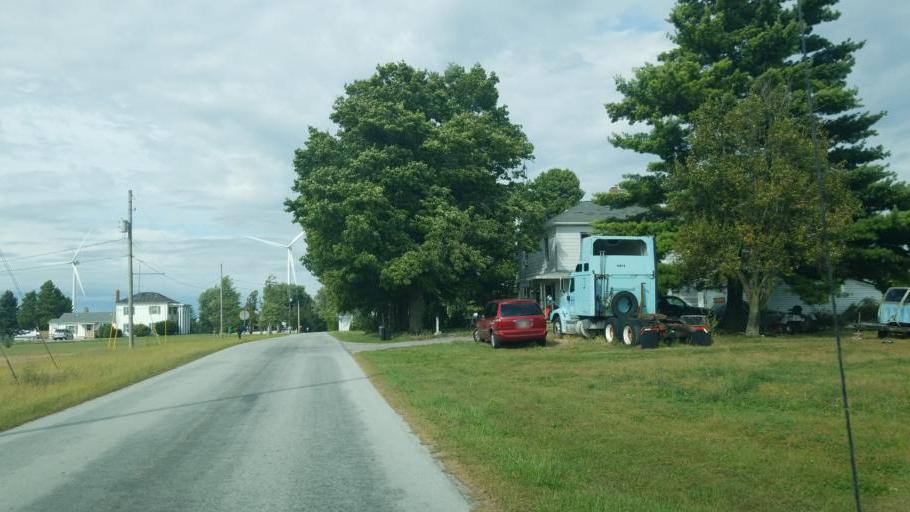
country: US
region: Ohio
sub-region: Hancock County
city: Arlington
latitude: 40.7880
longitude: -83.6518
